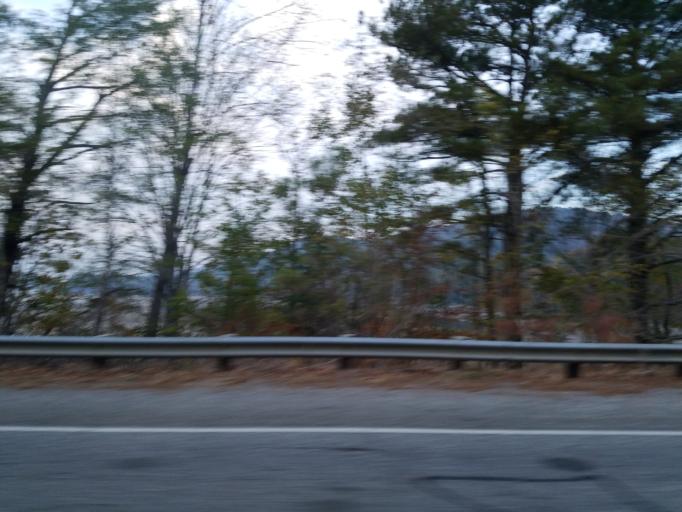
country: US
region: Georgia
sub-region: Murray County
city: Chatsworth
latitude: 34.5889
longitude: -84.6692
